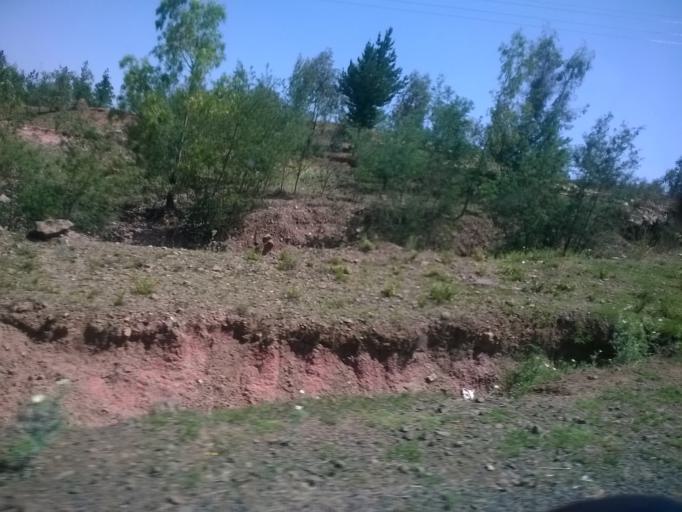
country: LS
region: Berea
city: Teyateyaneng
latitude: -29.1173
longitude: 27.7989
